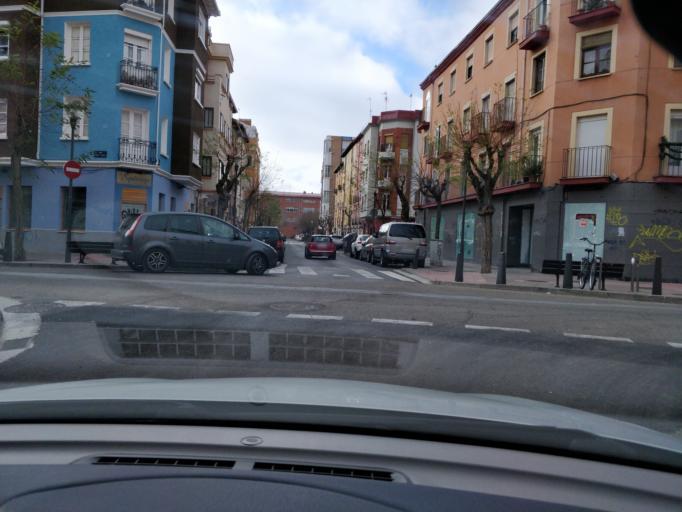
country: ES
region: Castille and Leon
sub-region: Provincia de Burgos
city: Burgos
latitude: 42.3487
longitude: -3.6976
